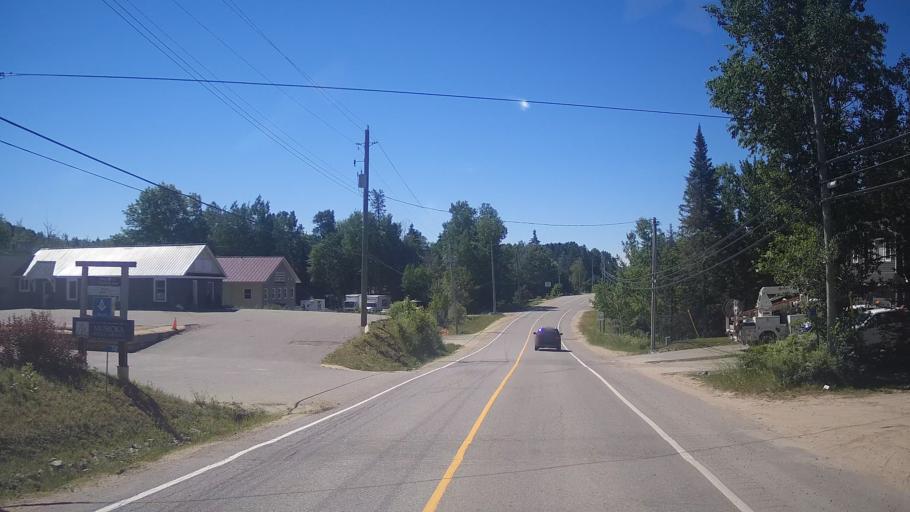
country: CA
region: Ontario
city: Huntsville
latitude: 45.3524
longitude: -79.2018
